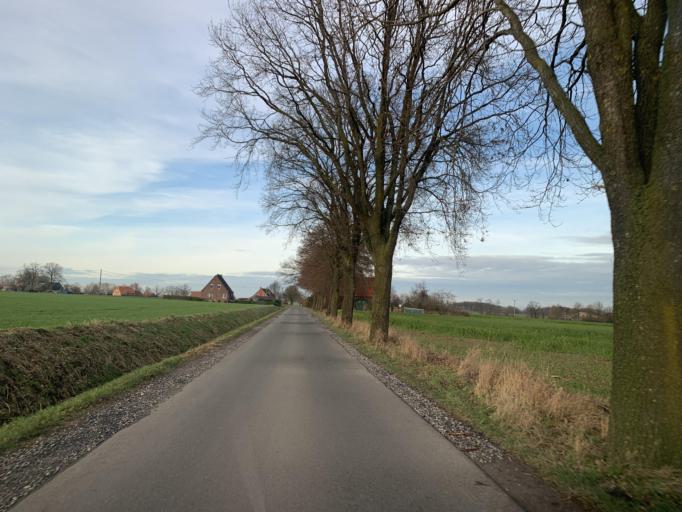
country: DE
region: North Rhine-Westphalia
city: Ludinghausen
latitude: 51.7762
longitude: 7.3818
